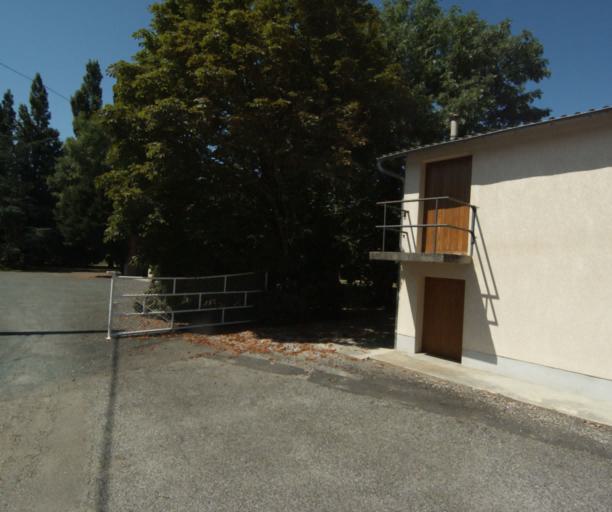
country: FR
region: Midi-Pyrenees
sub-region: Departement de la Haute-Garonne
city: Revel
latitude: 43.4717
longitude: 2.0079
